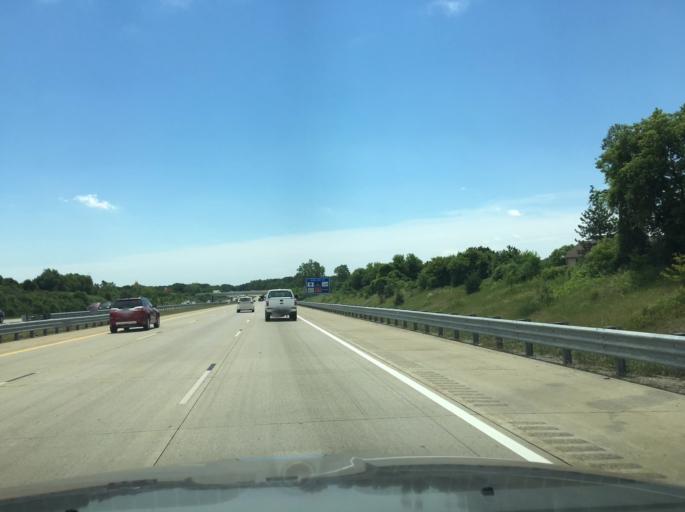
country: US
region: Michigan
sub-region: Oakland County
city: Rochester Hills
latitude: 42.6391
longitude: -83.1493
